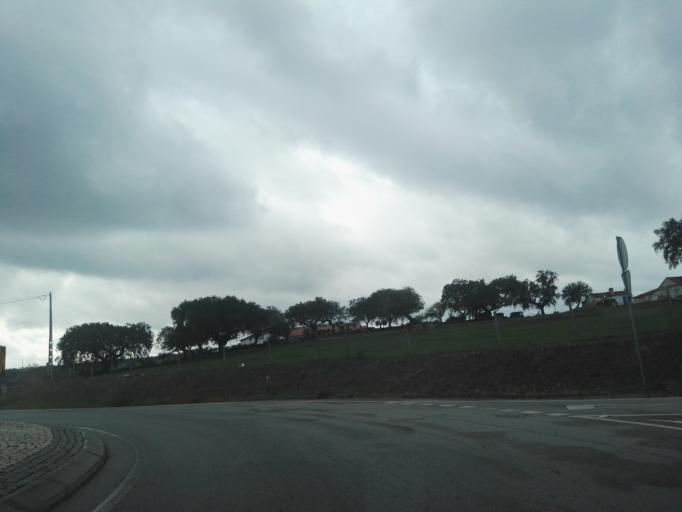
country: PT
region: Portalegre
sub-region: Arronches
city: Arronches
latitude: 39.1240
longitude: -7.2957
